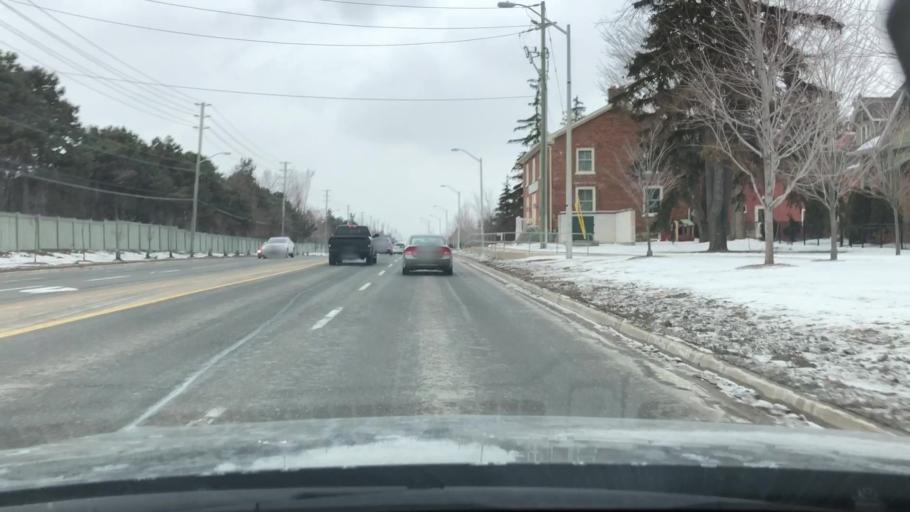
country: CA
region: Ontario
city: Markham
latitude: 43.8890
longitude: -79.2373
